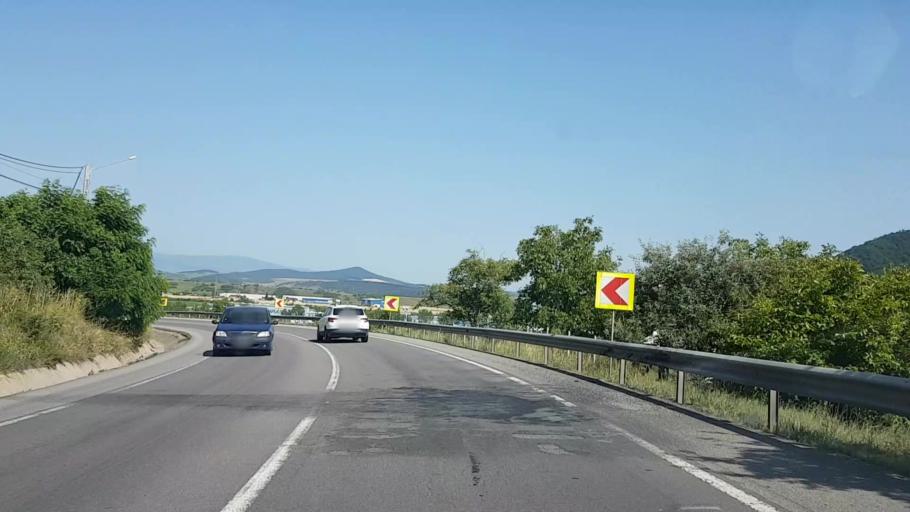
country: RO
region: Bistrita-Nasaud
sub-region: Comuna Sieu-Magherus
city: Sieu-Magherus
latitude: 47.0637
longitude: 24.4154
